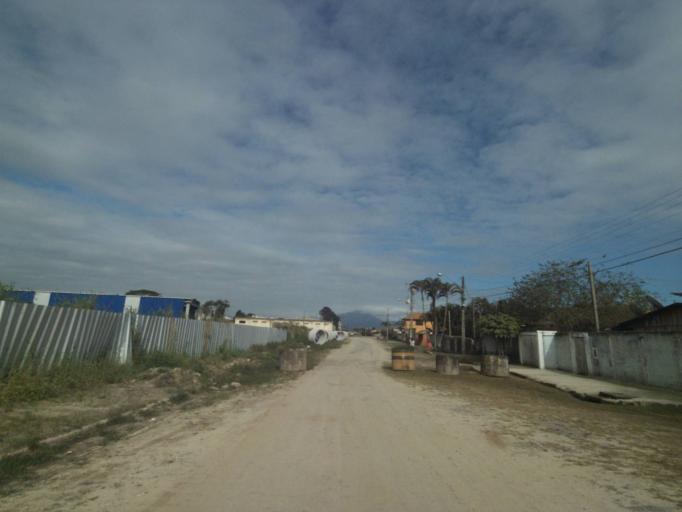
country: BR
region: Parana
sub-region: Paranagua
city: Paranagua
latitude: -25.5064
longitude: -48.5284
